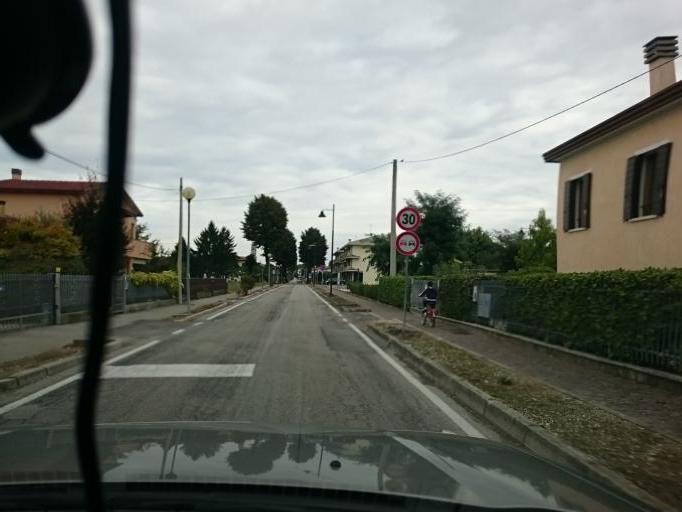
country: IT
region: Veneto
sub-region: Provincia di Padova
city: Saccolongo
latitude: 45.4094
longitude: 11.7387
